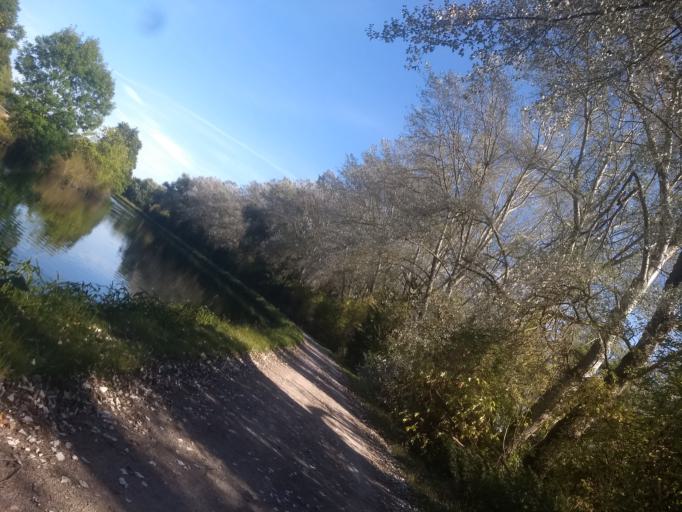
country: FR
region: Nord-Pas-de-Calais
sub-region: Departement du Pas-de-Calais
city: Roeux
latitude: 50.2911
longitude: 2.8895
